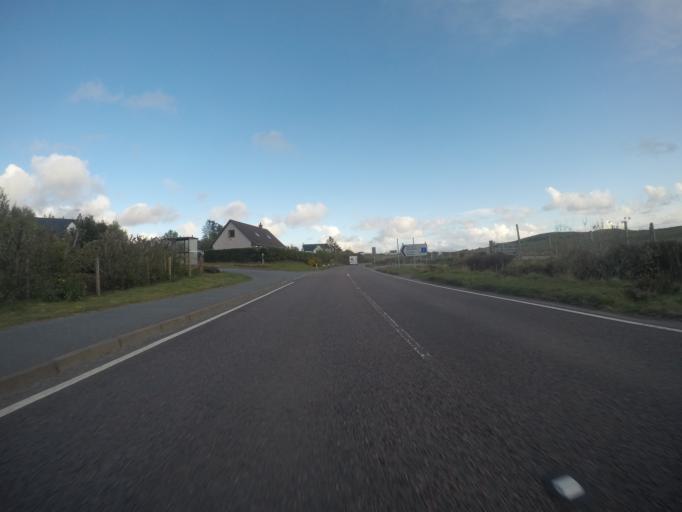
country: GB
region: Scotland
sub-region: Highland
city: Portree
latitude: 57.4809
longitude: -6.3015
